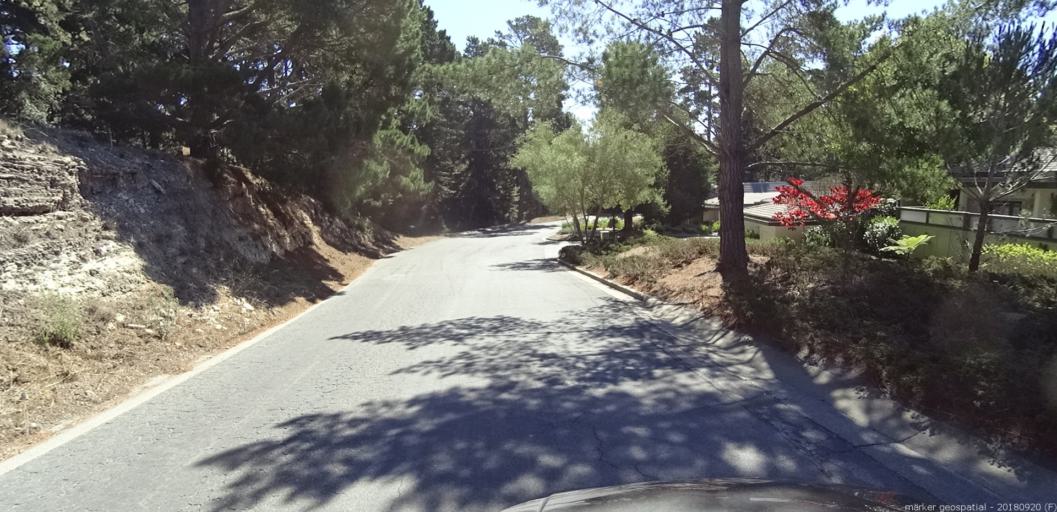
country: US
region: California
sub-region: Monterey County
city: Carmel-by-the-Sea
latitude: 36.5667
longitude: -121.9082
